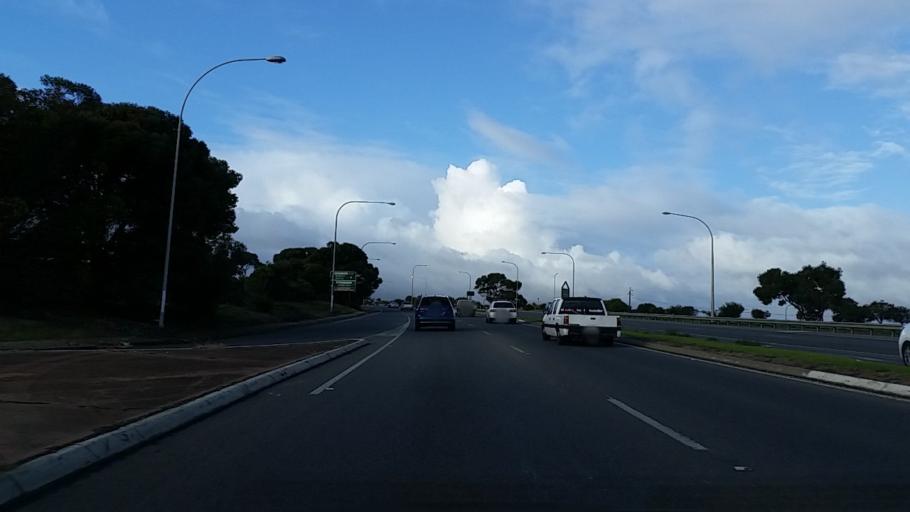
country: AU
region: South Australia
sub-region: Onkaparinga
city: Reynella
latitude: -35.0853
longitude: 138.5066
